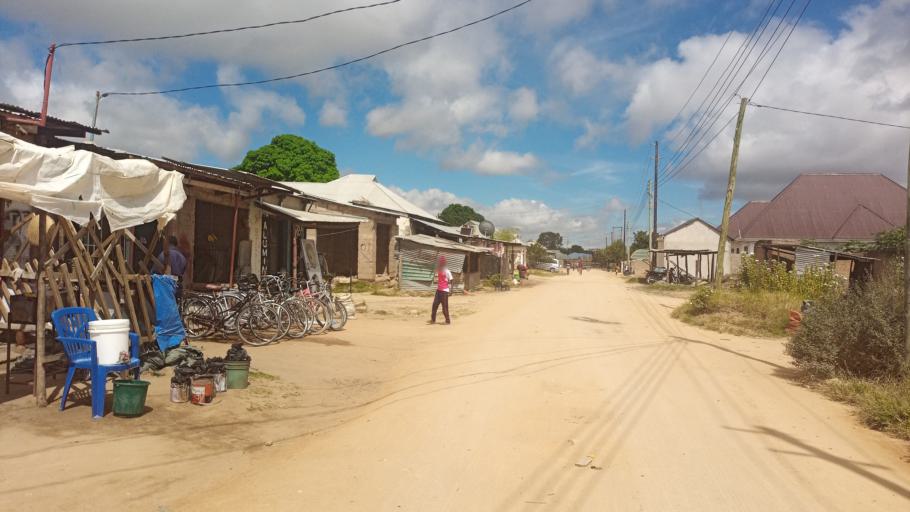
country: TZ
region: Dodoma
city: Kisasa
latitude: -6.1753
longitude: 35.7724
